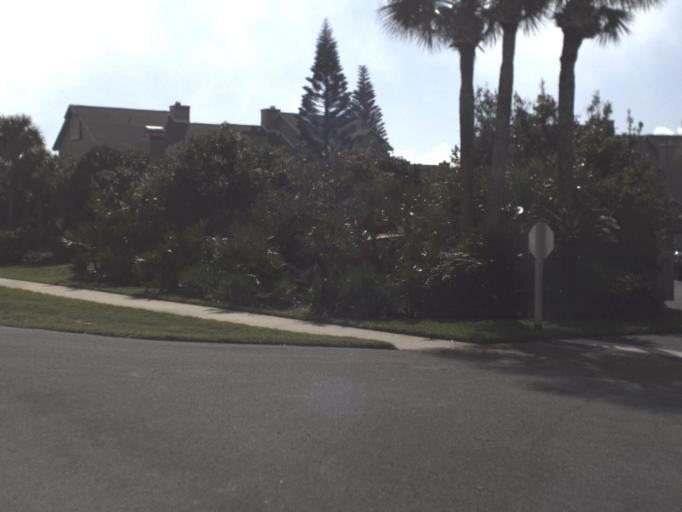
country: US
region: Florida
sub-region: Volusia County
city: Edgewater
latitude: 29.0002
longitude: -80.8739
